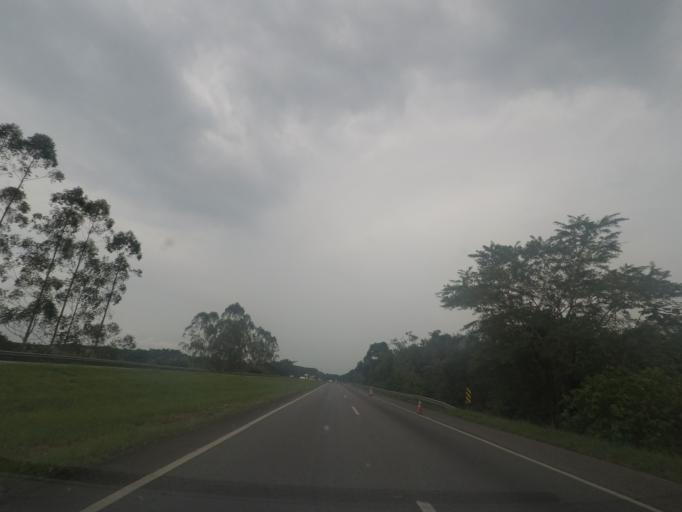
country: BR
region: Sao Paulo
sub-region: Registro
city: Registro
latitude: -24.5898
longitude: -47.8809
